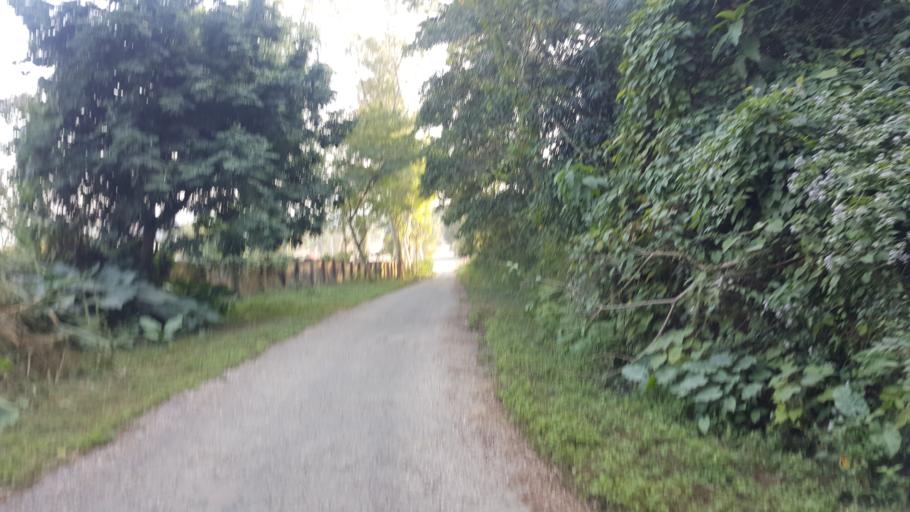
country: VN
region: Hoa Binh
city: Luong Son
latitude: 20.9131
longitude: 105.5763
